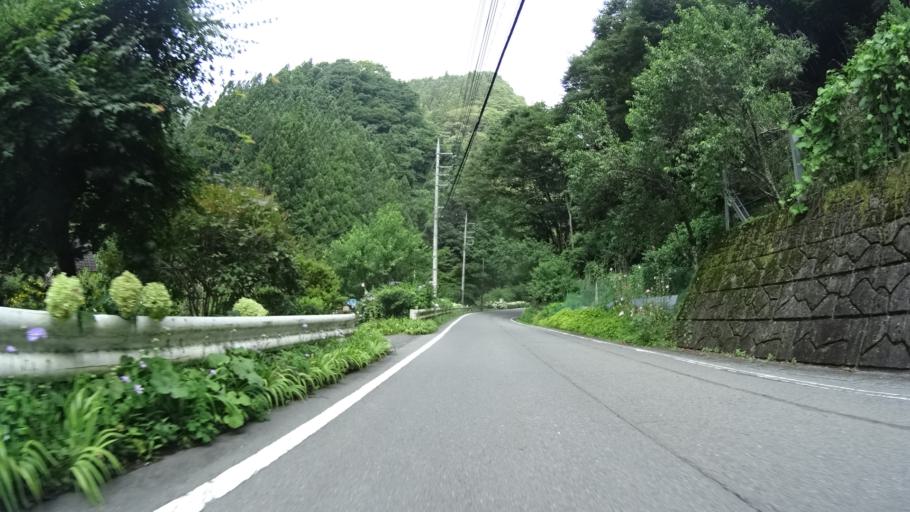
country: JP
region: Gunma
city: Tomioka
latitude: 36.0668
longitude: 138.8315
